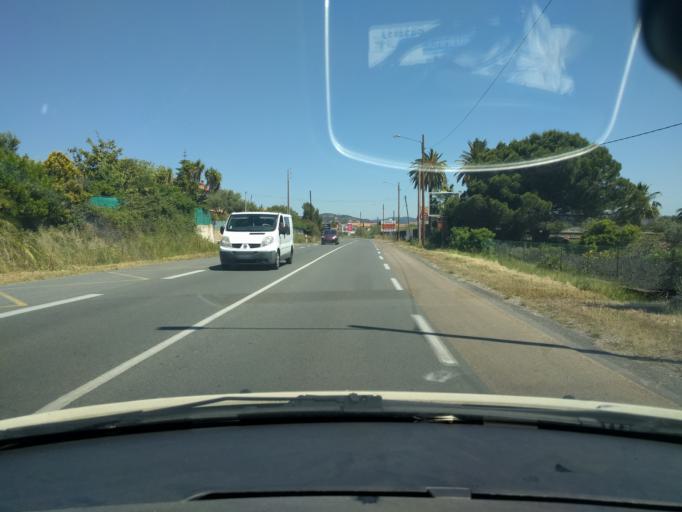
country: FR
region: Provence-Alpes-Cote d'Azur
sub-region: Departement du Var
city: Hyeres
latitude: 43.0945
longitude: 6.1310
